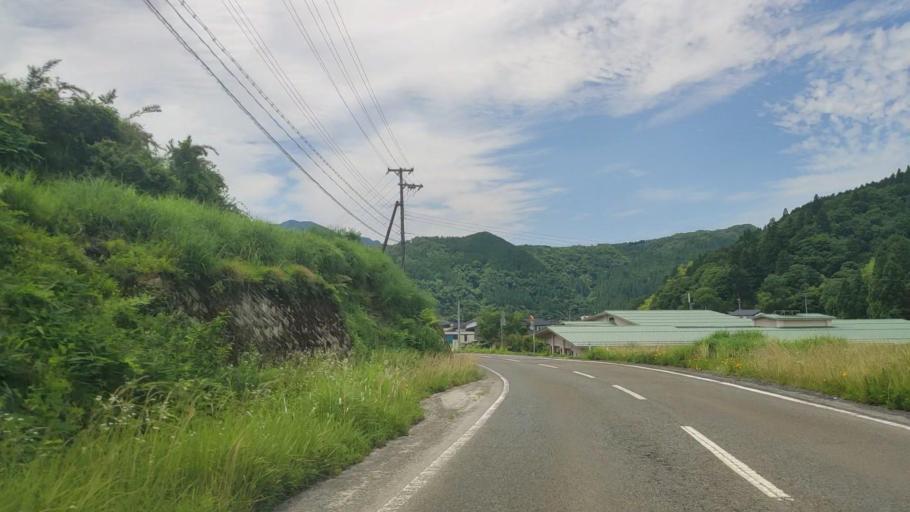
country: JP
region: Hyogo
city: Toyooka
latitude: 35.4762
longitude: 134.6009
